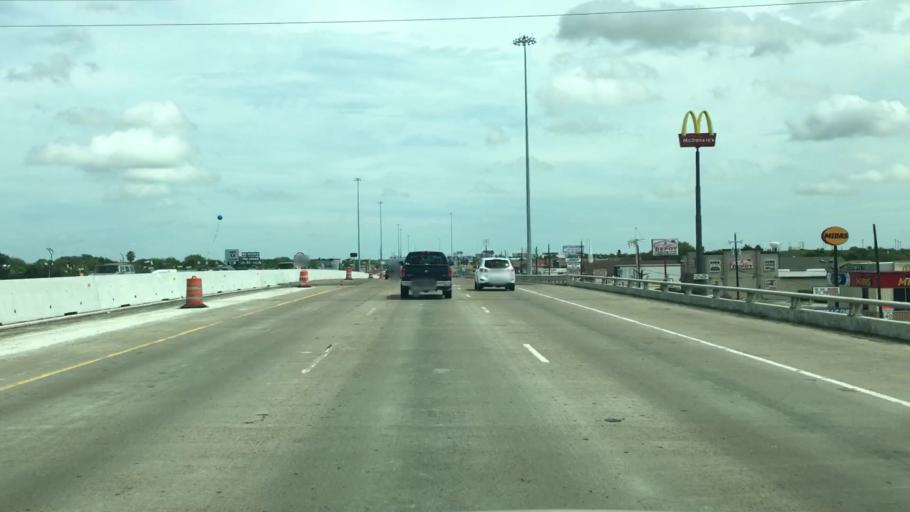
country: US
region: Texas
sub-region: Nueces County
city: Corpus Christi
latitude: 27.7285
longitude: -97.4131
